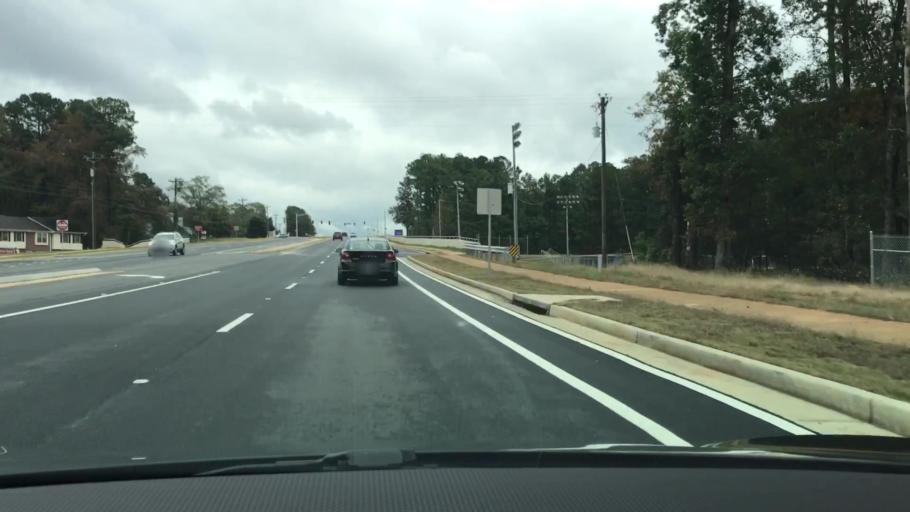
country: US
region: Georgia
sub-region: Oconee County
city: Watkinsville
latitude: 33.8768
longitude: -83.4480
